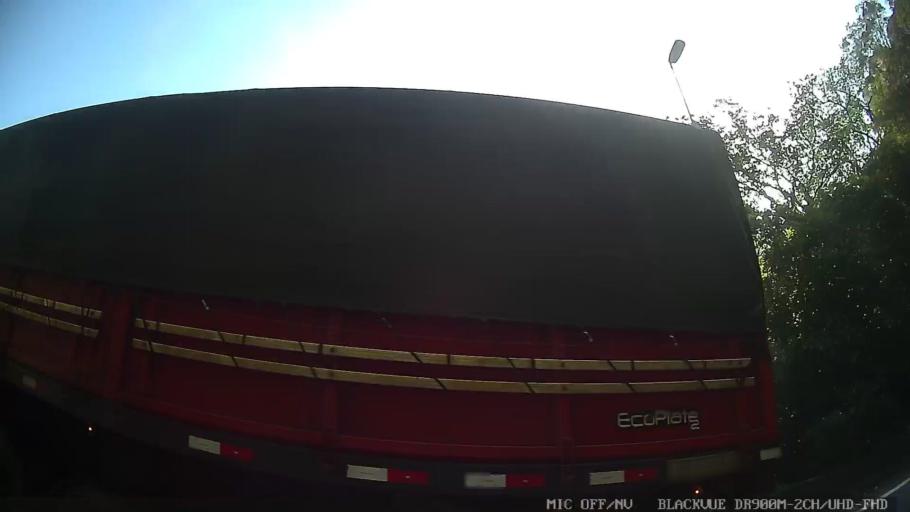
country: BR
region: Sao Paulo
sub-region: Cubatao
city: Cubatao
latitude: -23.8884
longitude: -46.4928
